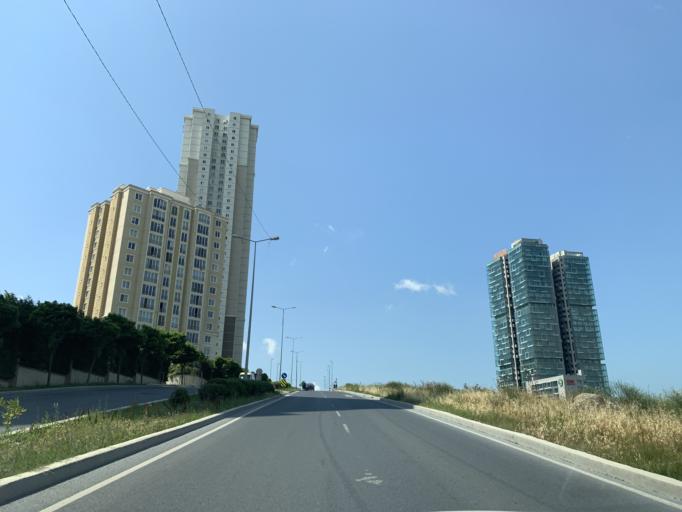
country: TR
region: Istanbul
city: Esenyurt
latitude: 41.0726
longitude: 28.6998
